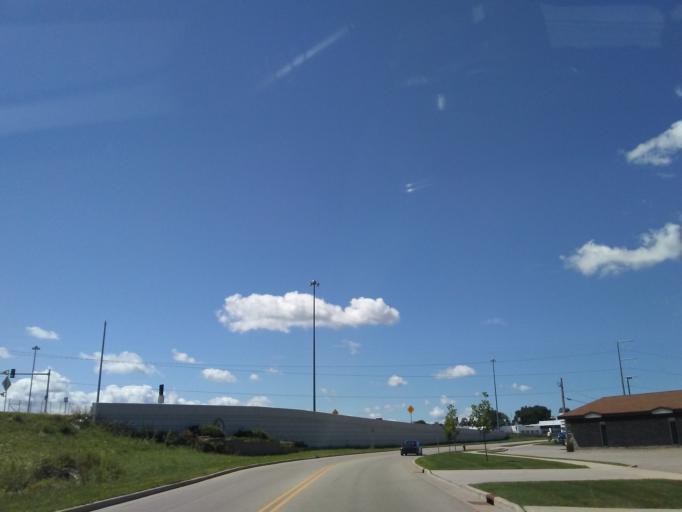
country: US
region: Wisconsin
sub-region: Dane County
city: Madison
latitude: 43.0361
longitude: -89.4065
